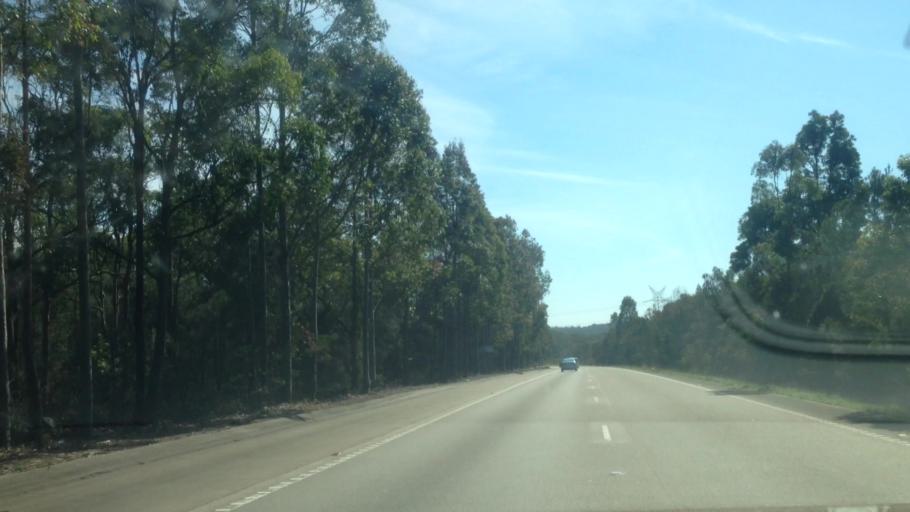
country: AU
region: New South Wales
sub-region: Lake Macquarie Shire
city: Fennell Bay
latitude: -32.9585
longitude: 151.5417
